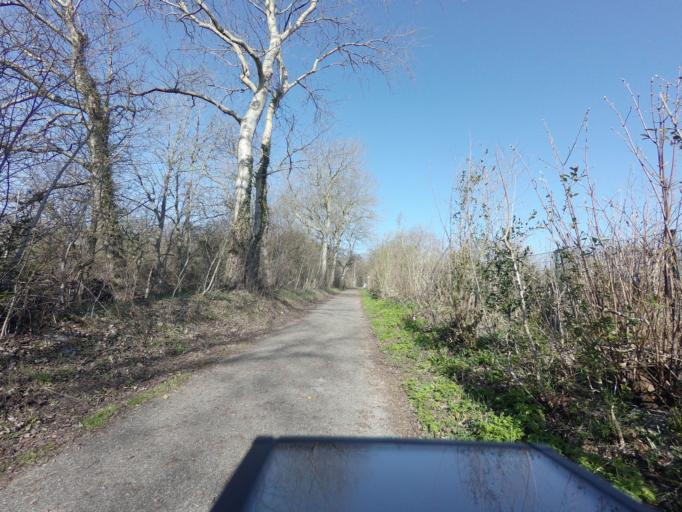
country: NL
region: Zeeland
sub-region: Schouwen-Duiveland
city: Renesse
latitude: 51.7267
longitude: 3.7649
